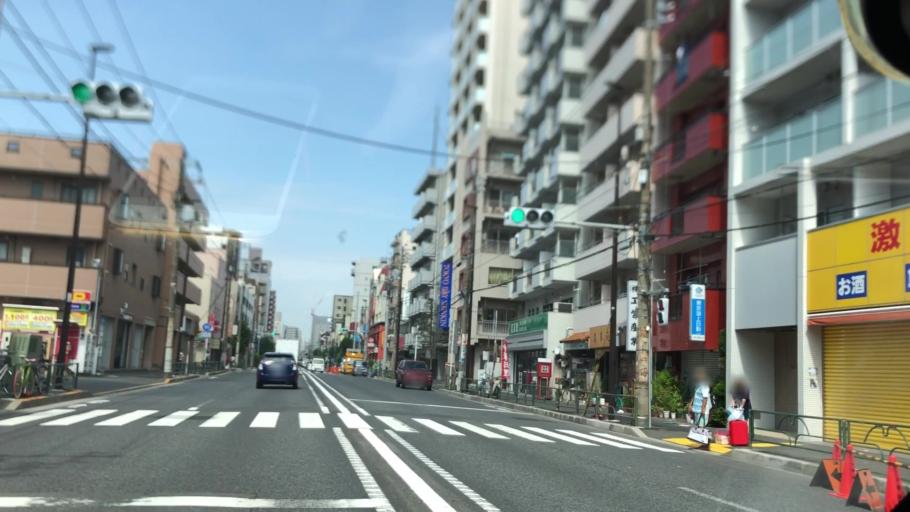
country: JP
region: Tokyo
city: Urayasu
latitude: 35.6902
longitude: 139.8406
